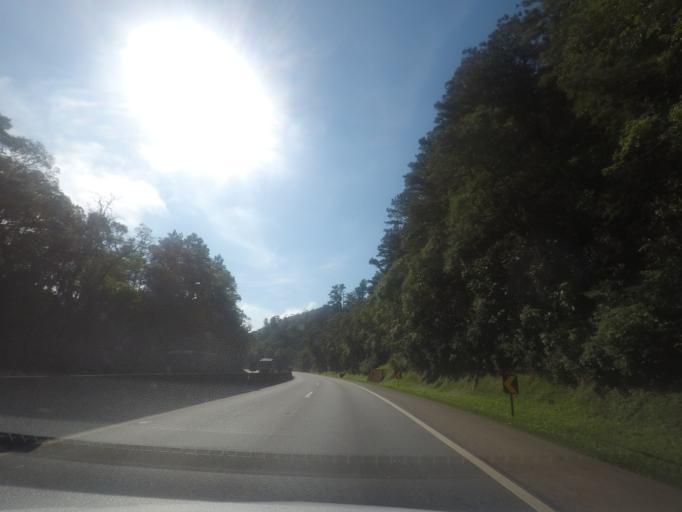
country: BR
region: Parana
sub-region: Piraquara
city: Piraquara
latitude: -25.5963
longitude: -48.8996
